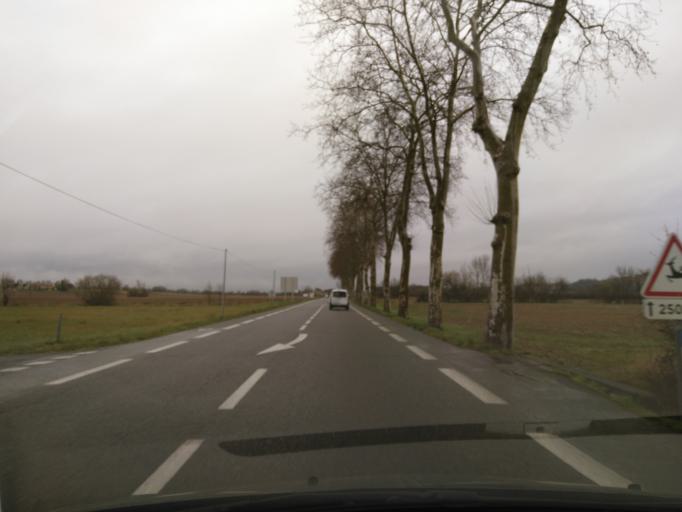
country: FR
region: Midi-Pyrenees
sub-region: Departement de la Haute-Garonne
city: Rieux-Volvestre
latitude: 43.2685
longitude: 1.1967
